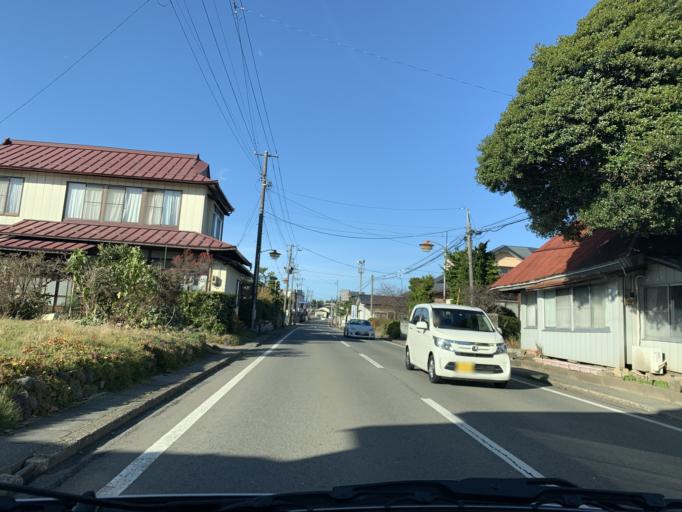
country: JP
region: Iwate
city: Mizusawa
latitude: 39.1993
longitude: 141.1175
